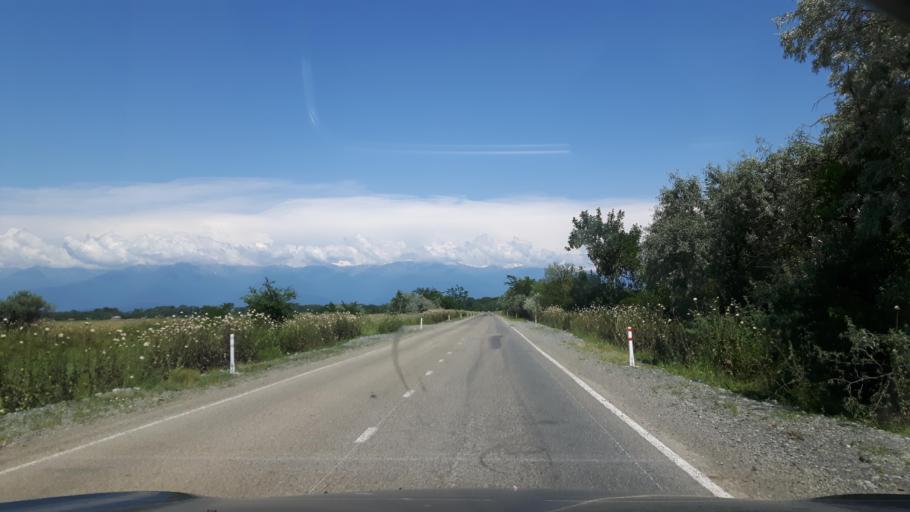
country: GE
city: Tsnori
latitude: 41.6578
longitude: 46.0667
